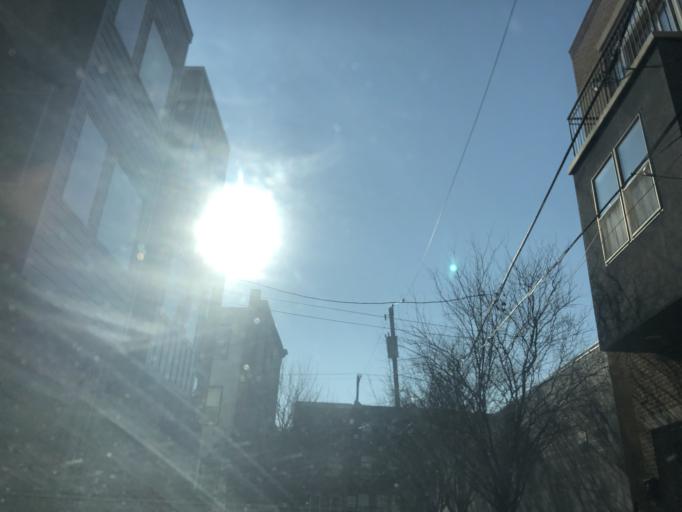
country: US
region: Pennsylvania
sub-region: Philadelphia County
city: Philadelphia
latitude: 39.9418
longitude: -75.1702
